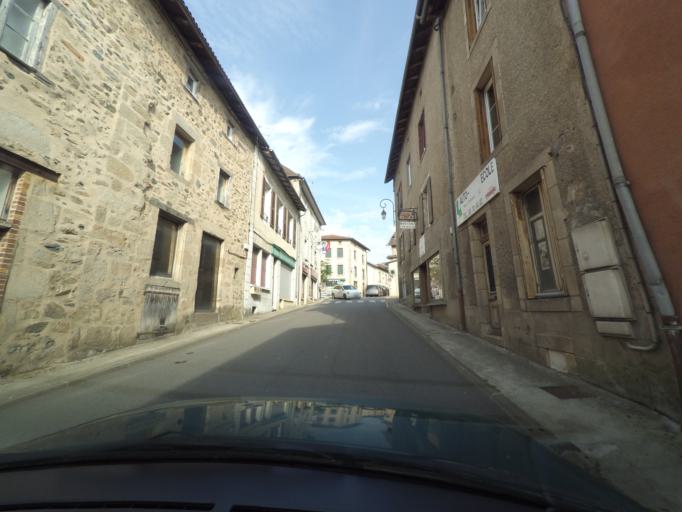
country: FR
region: Limousin
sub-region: Departement de la Haute-Vienne
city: Saint-Laurent-sur-Gorre
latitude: 45.7698
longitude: 0.9569
